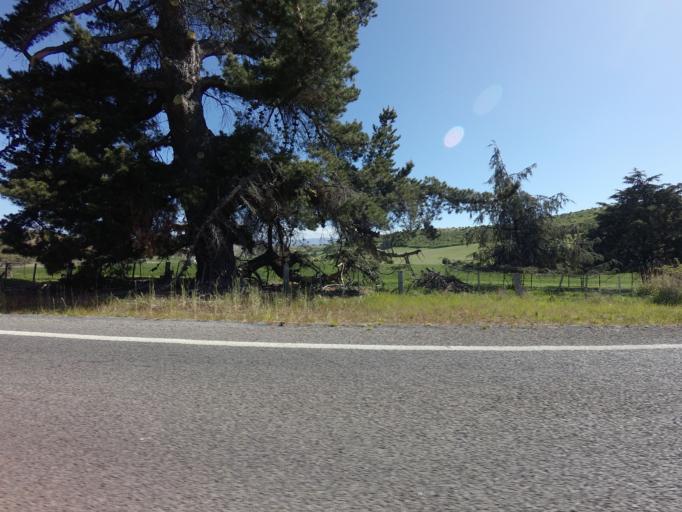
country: AU
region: Tasmania
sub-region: Derwent Valley
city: New Norfolk
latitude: -42.5659
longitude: 146.8805
